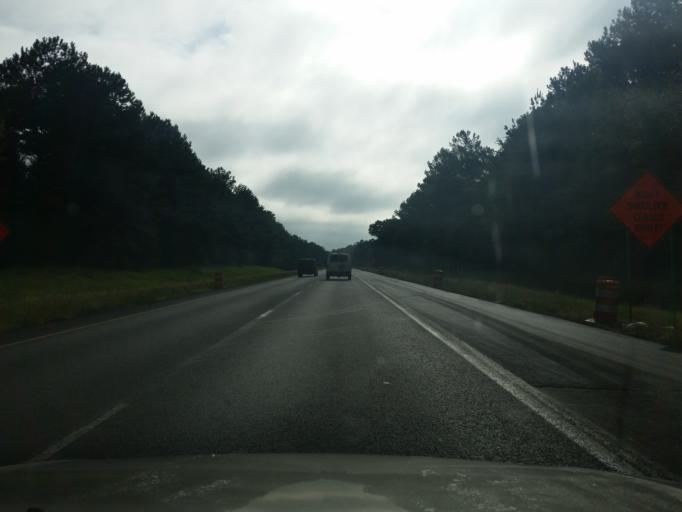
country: US
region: Alabama
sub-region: Baldwin County
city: Loxley
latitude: 30.6539
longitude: -87.7973
